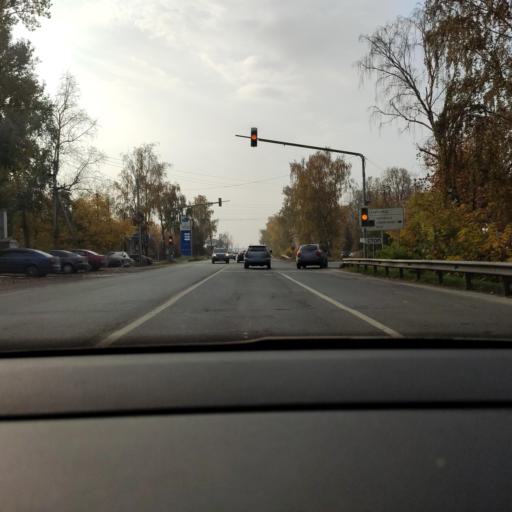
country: RU
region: Moskovskaya
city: Lesnyye Polyany
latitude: 55.9860
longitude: 37.8672
